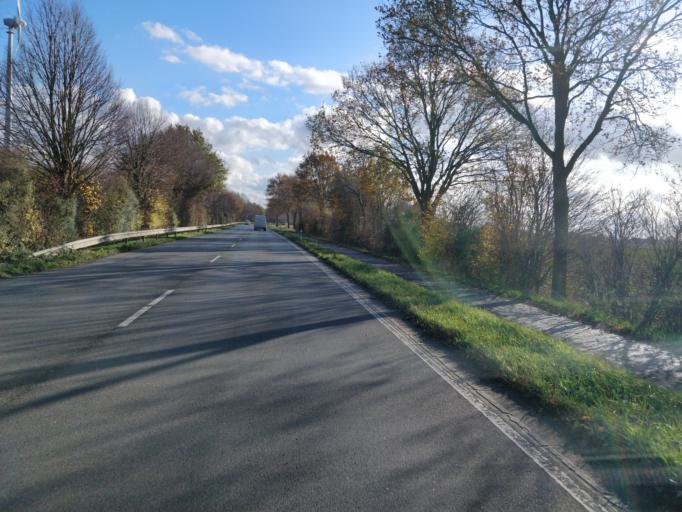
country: DE
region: North Rhine-Westphalia
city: Rees
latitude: 51.7843
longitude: 6.3749
